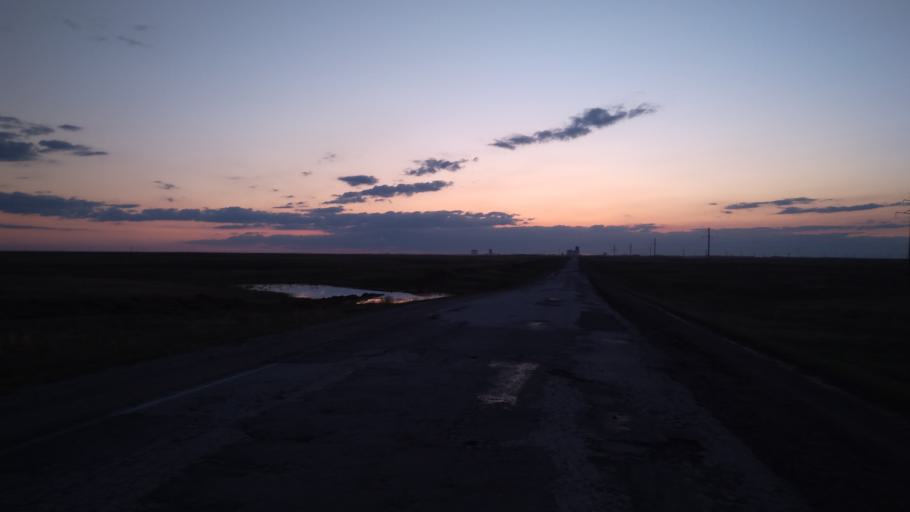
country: RU
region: Chelyabinsk
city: Troitsk
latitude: 54.0892
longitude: 61.6506
